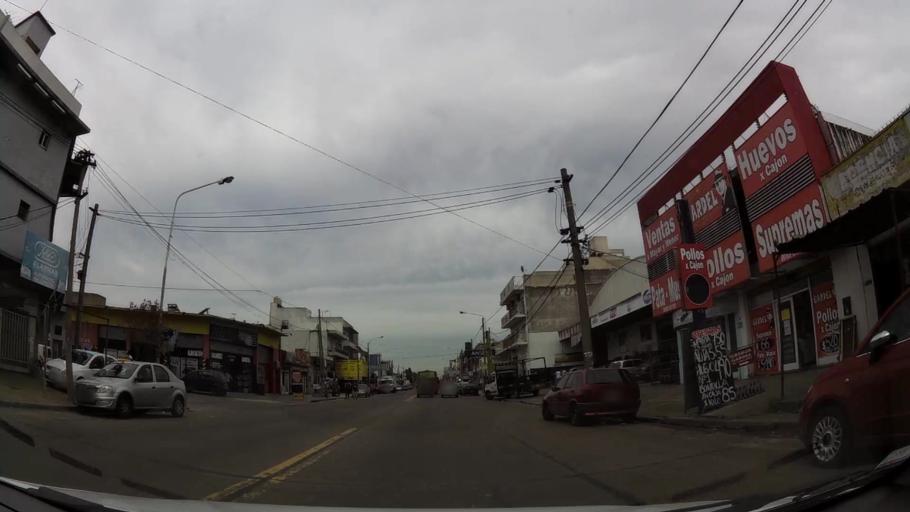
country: AR
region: Buenos Aires
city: San Justo
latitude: -34.6864
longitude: -58.5204
